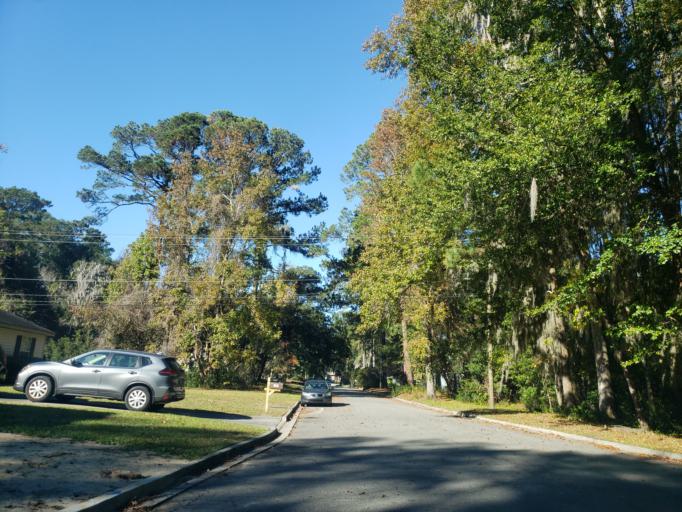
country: US
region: Georgia
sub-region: Chatham County
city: Isle of Hope
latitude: 31.9975
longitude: -81.1017
